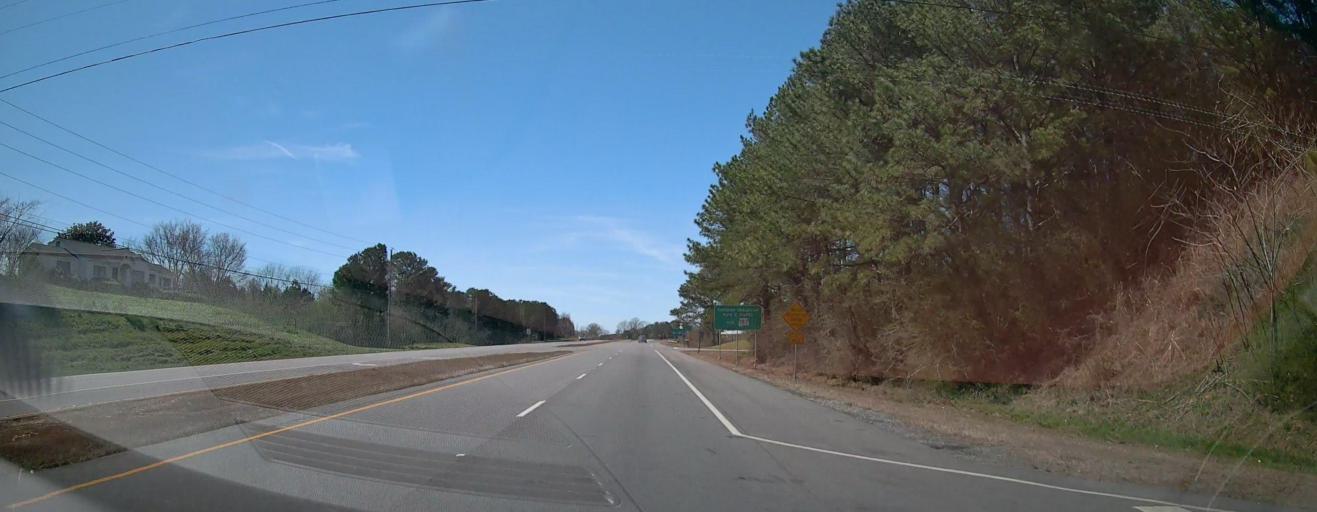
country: US
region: Alabama
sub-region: Cullman County
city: Cullman
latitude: 34.1833
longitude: -86.7806
